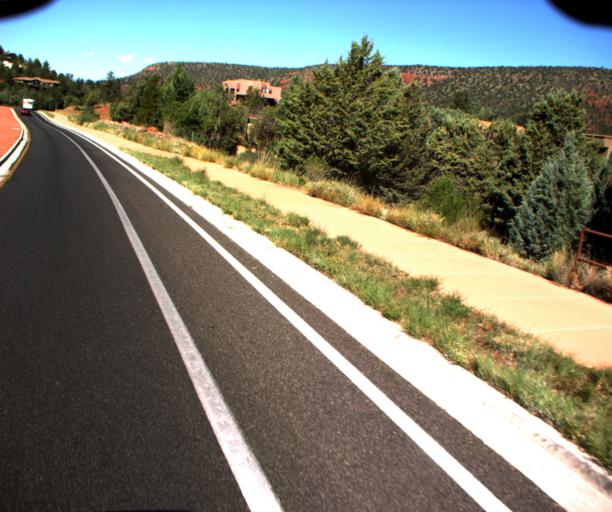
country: US
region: Arizona
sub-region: Coconino County
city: Sedona
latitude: 34.8446
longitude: -111.7686
